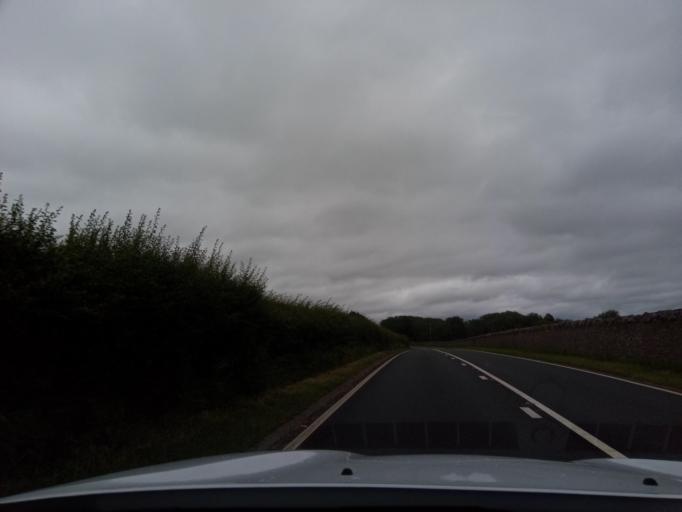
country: GB
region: Scotland
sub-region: The Scottish Borders
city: Lauder
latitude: 55.7280
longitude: -2.7627
